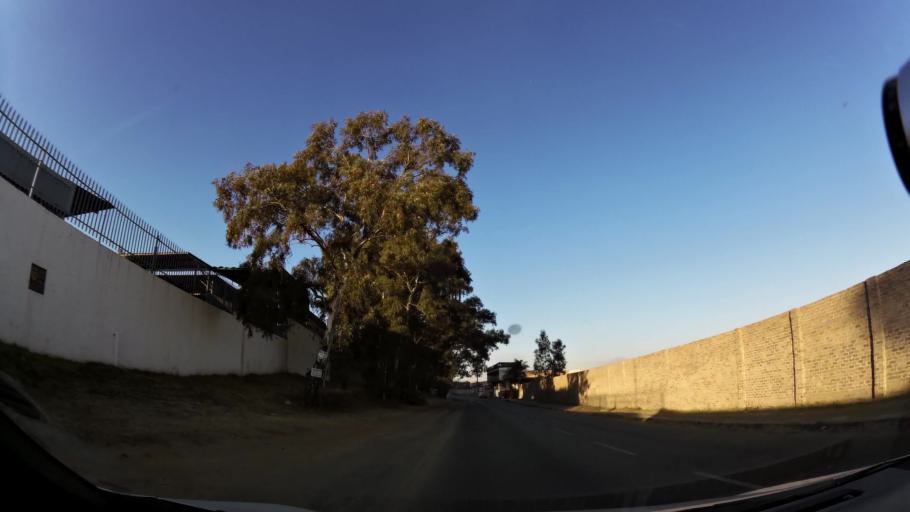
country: ZA
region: Gauteng
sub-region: Ekurhuleni Metropolitan Municipality
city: Germiston
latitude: -26.2531
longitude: 28.1388
